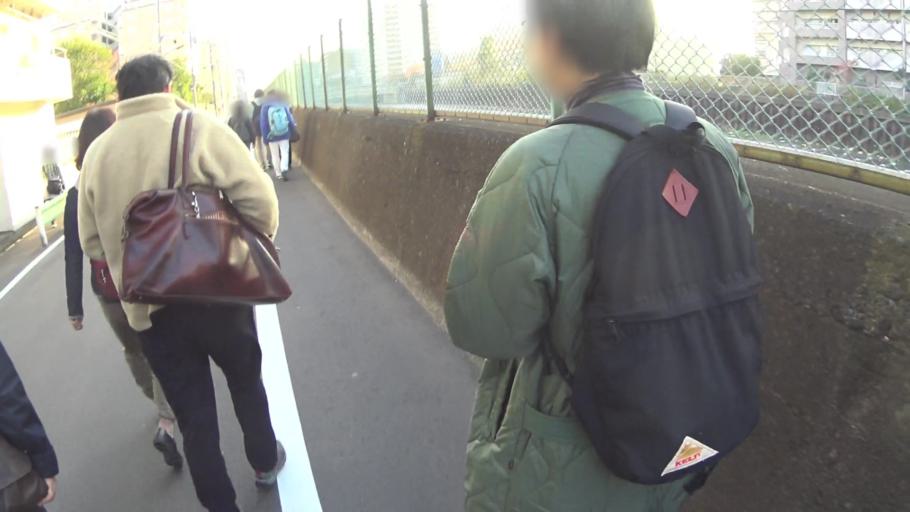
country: JP
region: Tokyo
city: Urayasu
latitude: 35.7061
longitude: 139.8186
